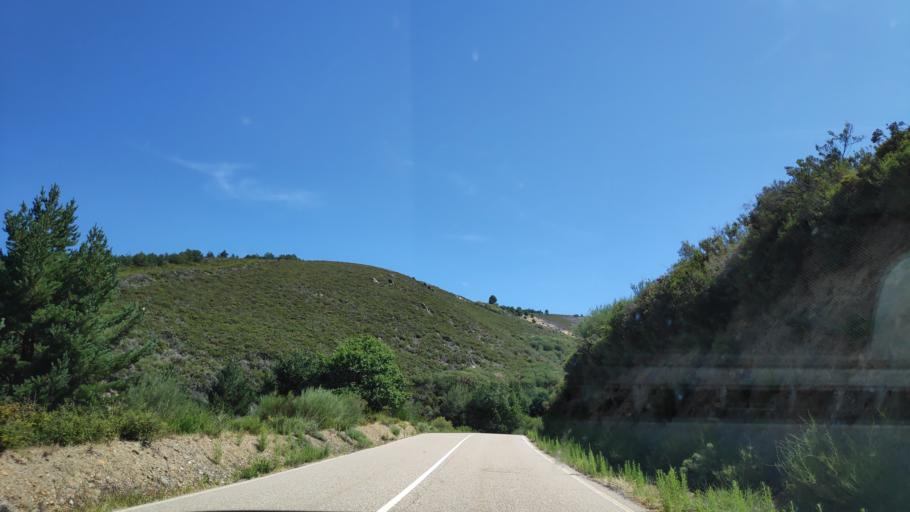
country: ES
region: Castille and Leon
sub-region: Provincia de Zamora
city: Requejo
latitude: 41.9807
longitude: -6.7113
